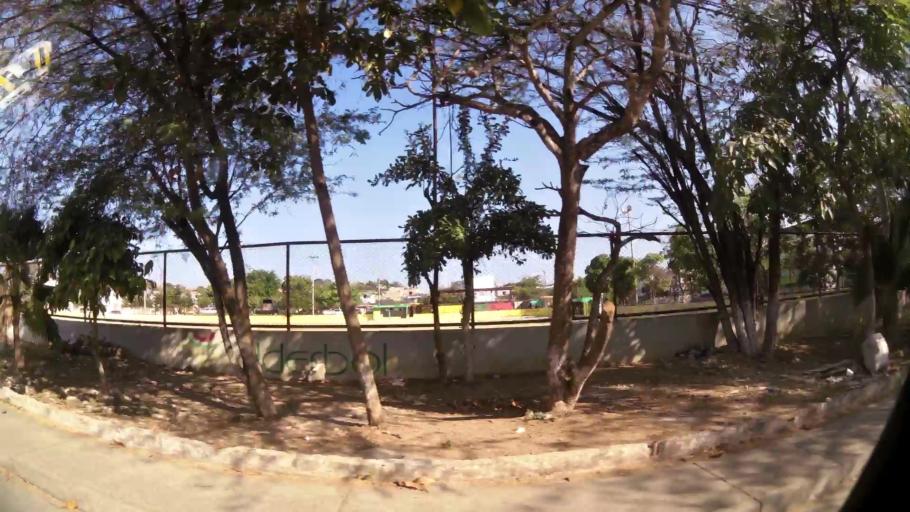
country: CO
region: Bolivar
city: Cartagena
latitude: 10.3911
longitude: -75.5052
